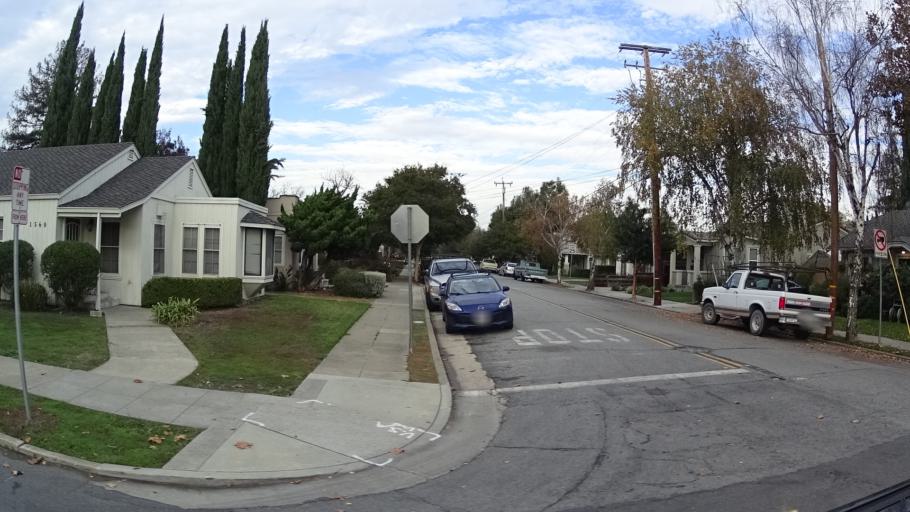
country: US
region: California
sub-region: Santa Clara County
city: Buena Vista
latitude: 37.3312
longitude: -121.9207
